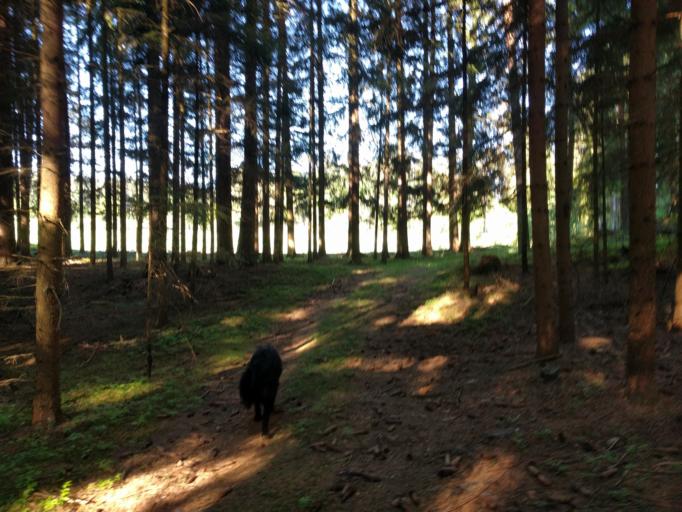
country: AT
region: Lower Austria
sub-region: Politischer Bezirk Zwettl
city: Langschlag
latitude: 48.5891
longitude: 14.9008
